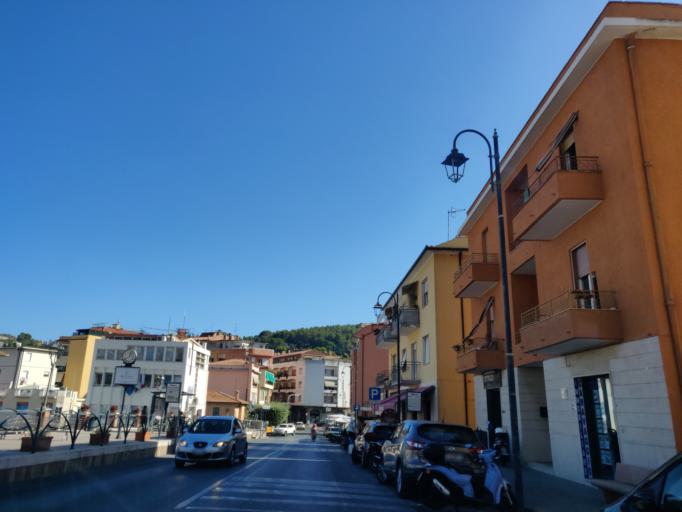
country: IT
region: Tuscany
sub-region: Provincia di Grosseto
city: Porto Ercole
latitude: 42.3946
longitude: 11.2037
